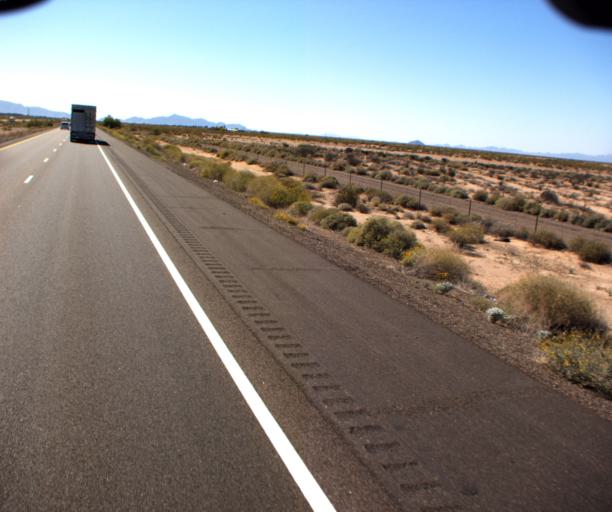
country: US
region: Arizona
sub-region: Yuma County
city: Wellton
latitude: 32.8143
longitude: -113.5051
